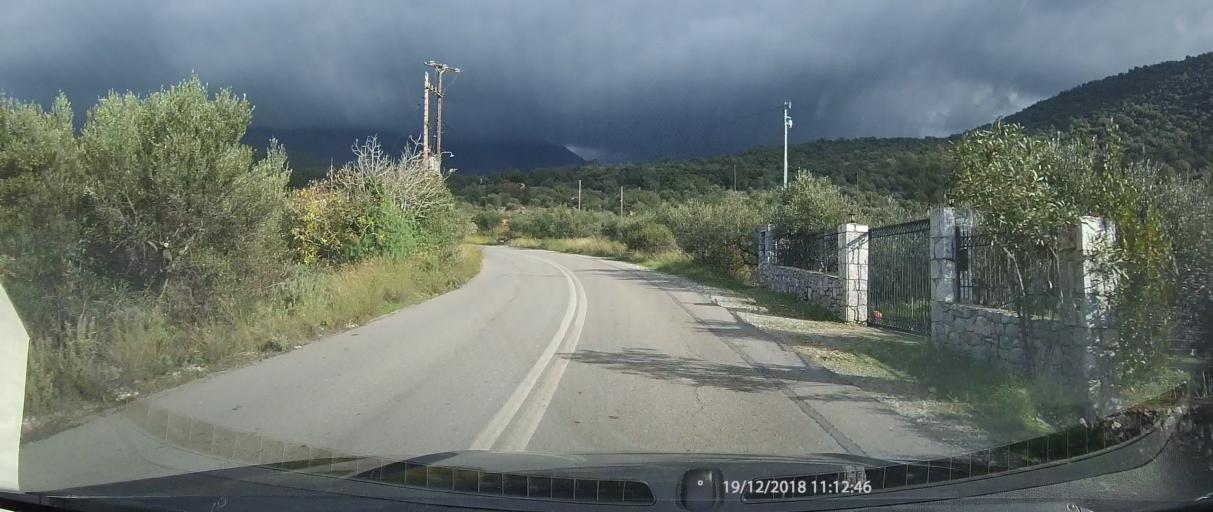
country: GR
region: Peloponnese
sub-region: Nomos Messinias
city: Kardamyli
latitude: 36.8220
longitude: 22.3086
